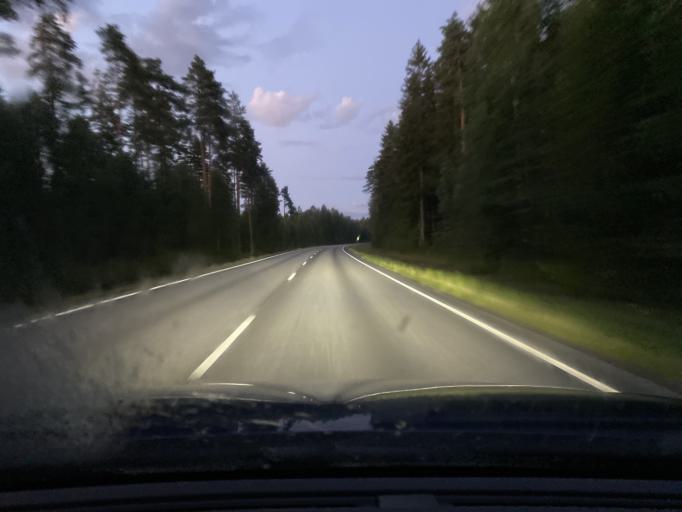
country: FI
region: Satakunta
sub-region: Pori
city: Vampula
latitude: 60.9507
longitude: 22.6993
